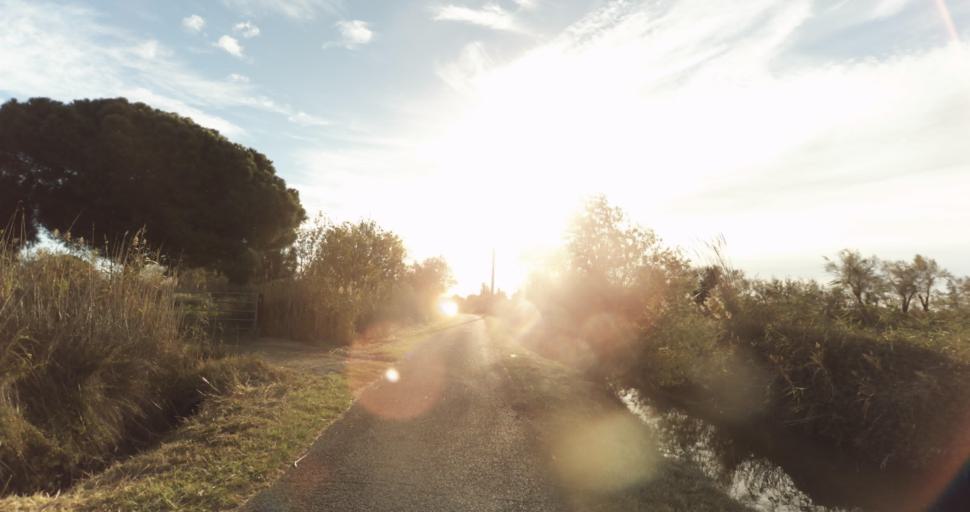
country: FR
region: Languedoc-Roussillon
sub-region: Departement du Gard
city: Aigues-Mortes
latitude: 43.5542
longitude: 4.2109
